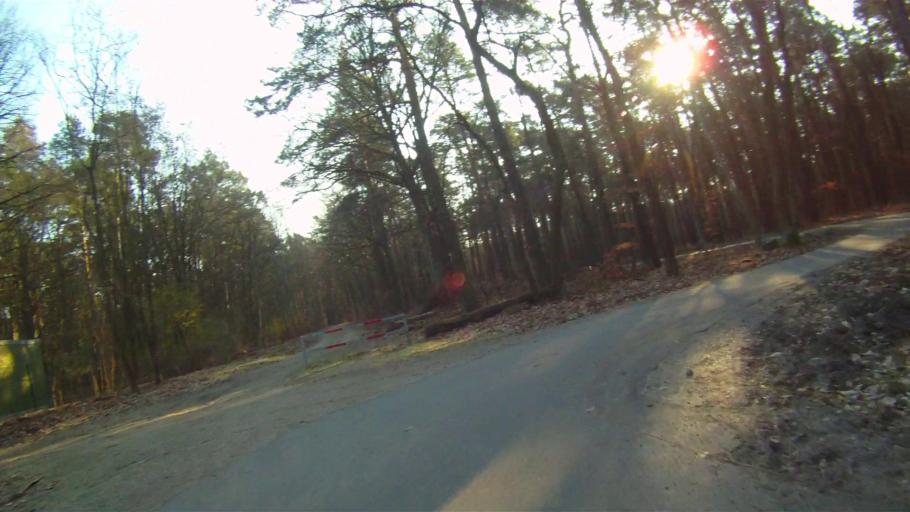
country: DE
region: Berlin
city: Muggelheim
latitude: 52.4236
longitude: 13.6481
